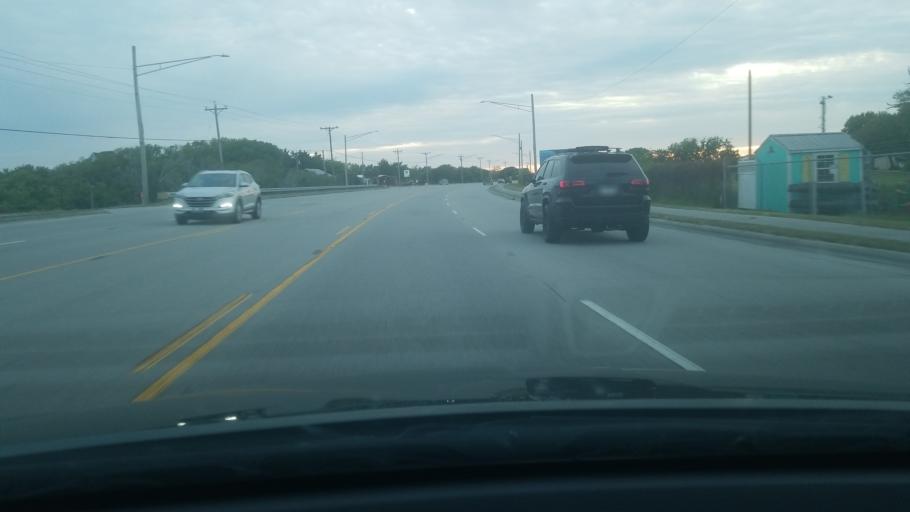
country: US
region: North Carolina
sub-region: Onslow County
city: Swansboro
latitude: 34.6769
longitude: -77.1010
